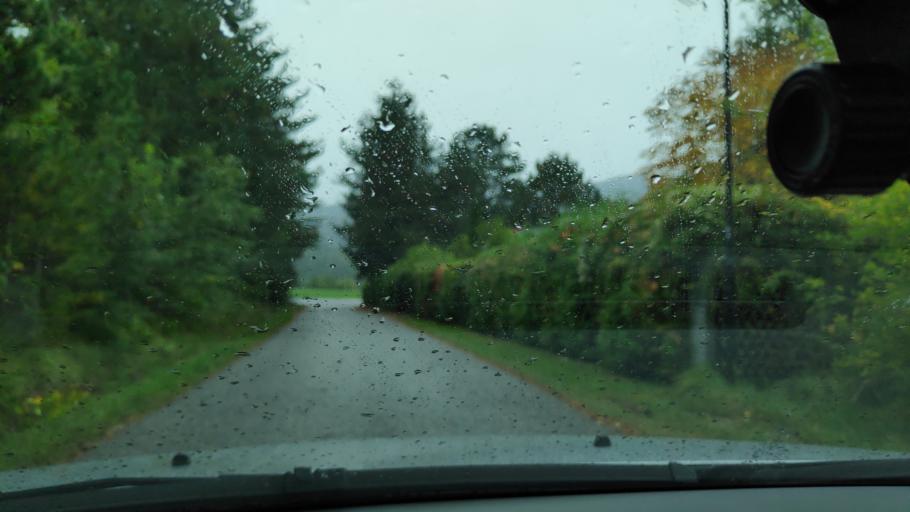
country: AT
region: Lower Austria
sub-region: Politischer Bezirk Neunkirchen
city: Grunbach am Schneeberg
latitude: 47.8009
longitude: 15.9926
